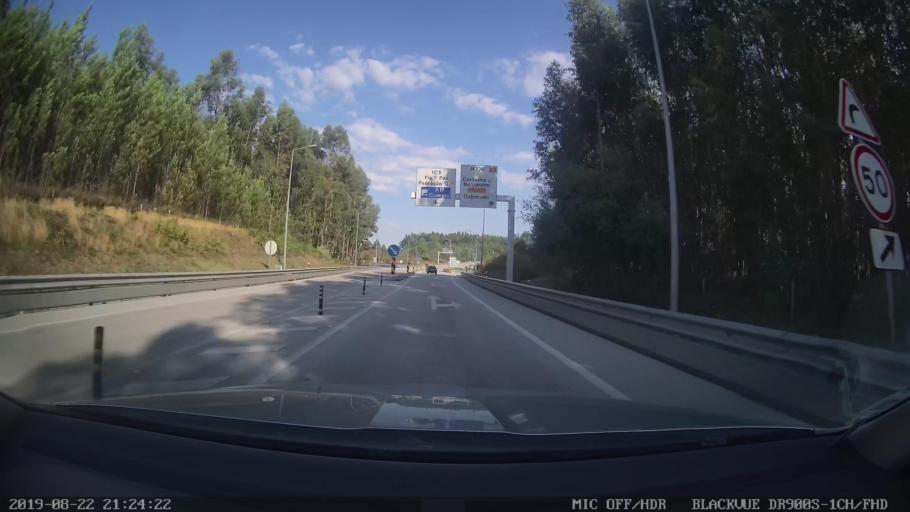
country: PT
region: Castelo Branco
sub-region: Serta
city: Serta
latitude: 39.8406
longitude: -8.1216
